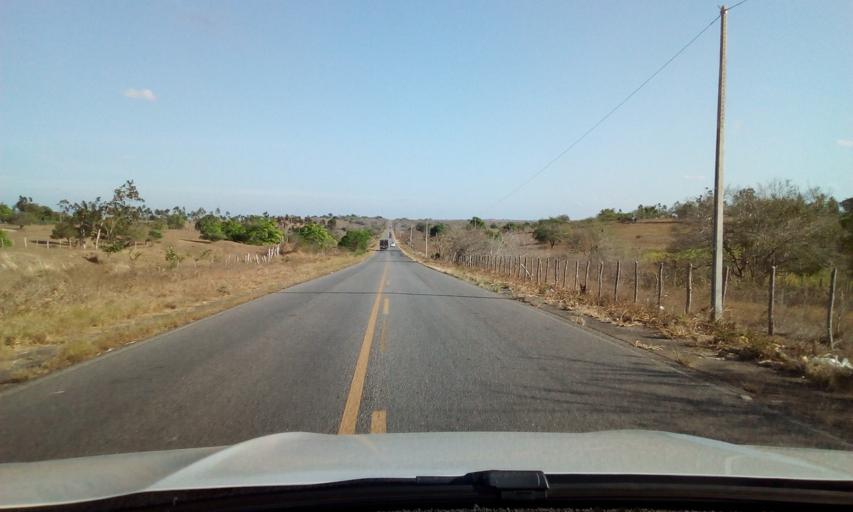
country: BR
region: Paraiba
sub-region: Guarabira
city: Guarabira
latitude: -6.9326
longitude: -35.4360
